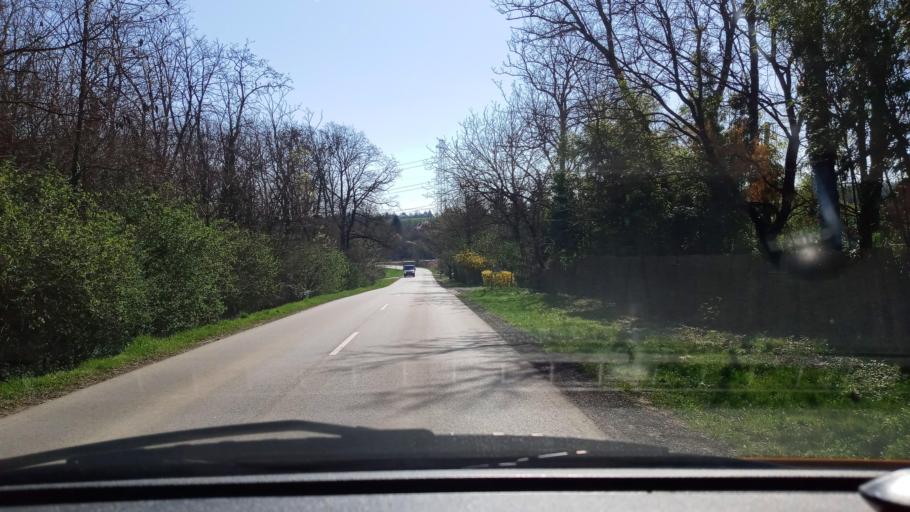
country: HU
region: Baranya
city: Kozarmisleny
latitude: 46.0849
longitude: 18.3046
